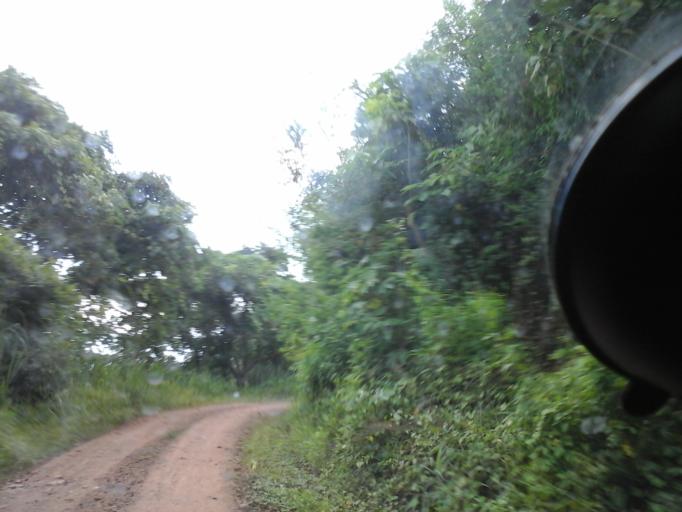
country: CO
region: Cesar
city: San Diego
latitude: 10.2675
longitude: -73.0781
